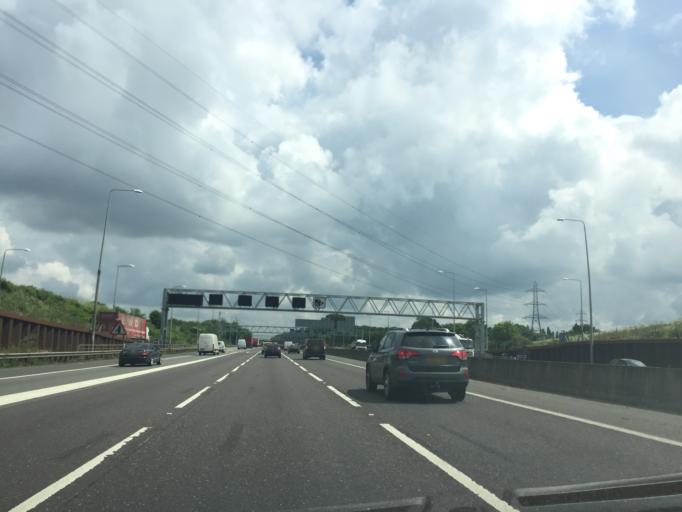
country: GB
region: England
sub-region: Hertfordshire
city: Abbots Langley
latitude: 51.7145
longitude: -0.3691
